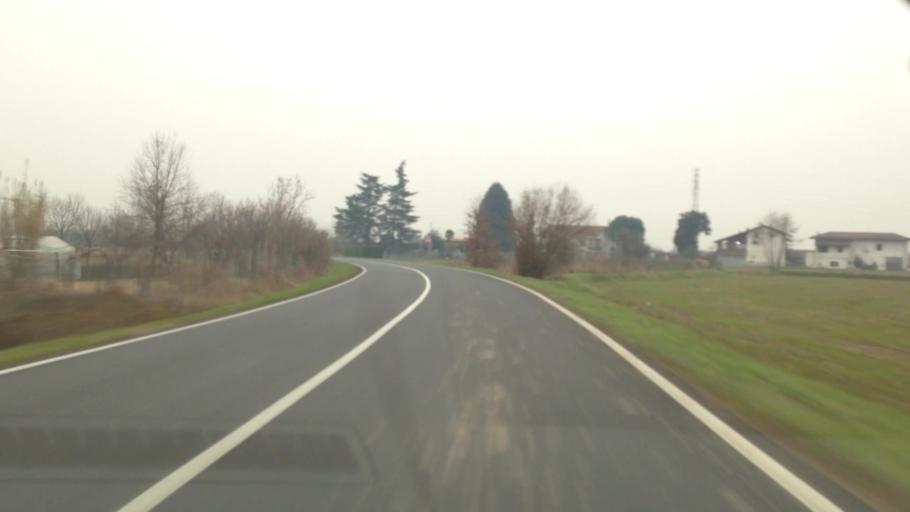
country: IT
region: Piedmont
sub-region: Provincia di Vercelli
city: Livorno Ferraris
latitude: 45.2845
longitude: 8.0626
